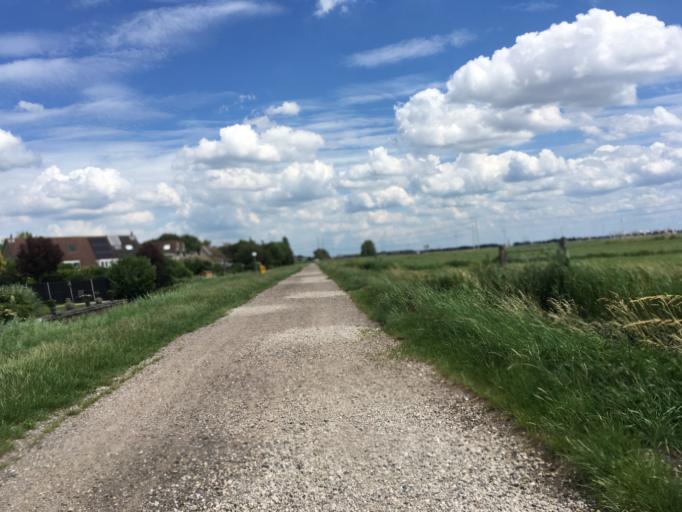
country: NL
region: North Holland
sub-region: Gemeente Haarlem
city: Haarlem
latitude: 52.4121
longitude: 4.6925
